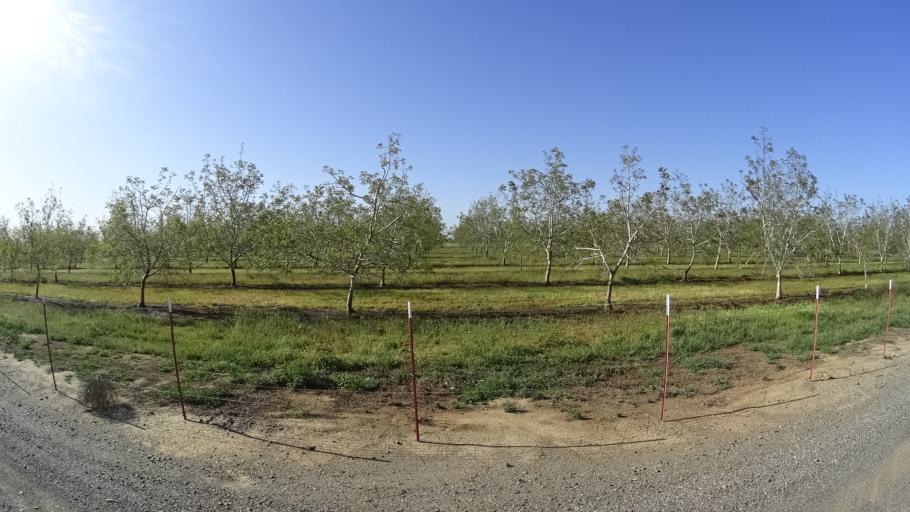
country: US
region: California
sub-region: Glenn County
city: Hamilton City
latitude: 39.6959
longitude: -122.0926
